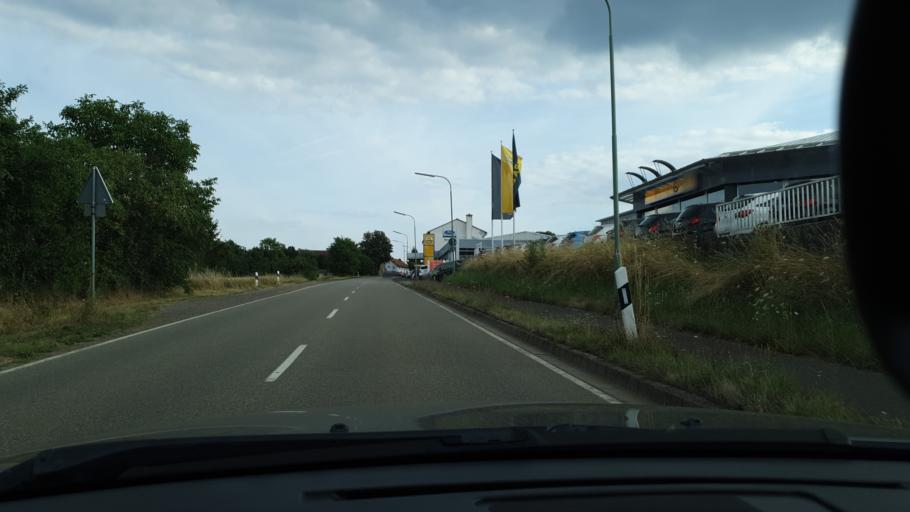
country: DE
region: Rheinland-Pfalz
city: Otterbach
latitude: 49.4715
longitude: 7.7614
